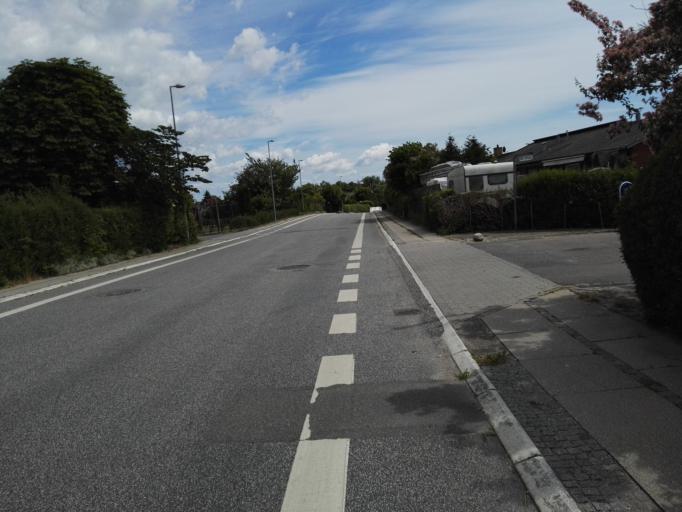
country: DK
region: Capital Region
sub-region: Egedal Kommune
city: Stenlose
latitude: 55.7615
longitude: 12.1907
